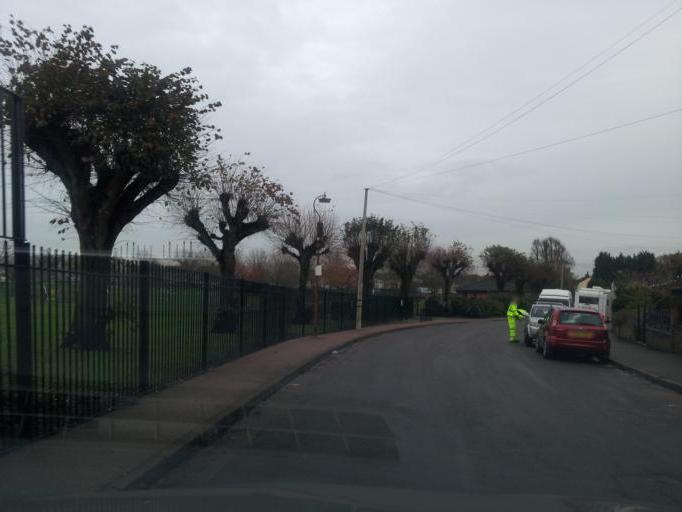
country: GB
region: England
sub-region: Essex
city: Colchester
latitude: 51.8794
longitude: 0.9176
